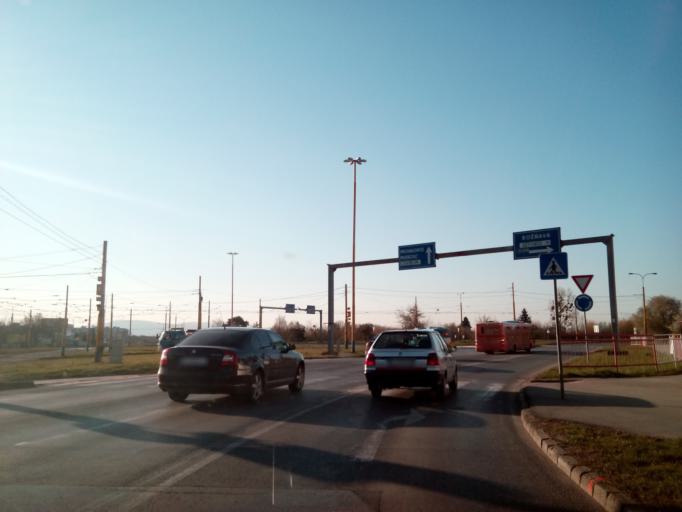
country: SK
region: Kosicky
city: Kosice
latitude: 48.7053
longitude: 21.2420
